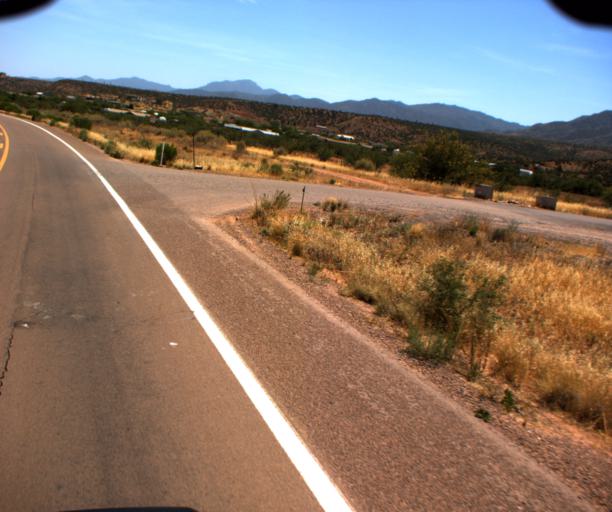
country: US
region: Arizona
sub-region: Gila County
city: Tonto Basin
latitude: 33.8509
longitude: -111.3107
